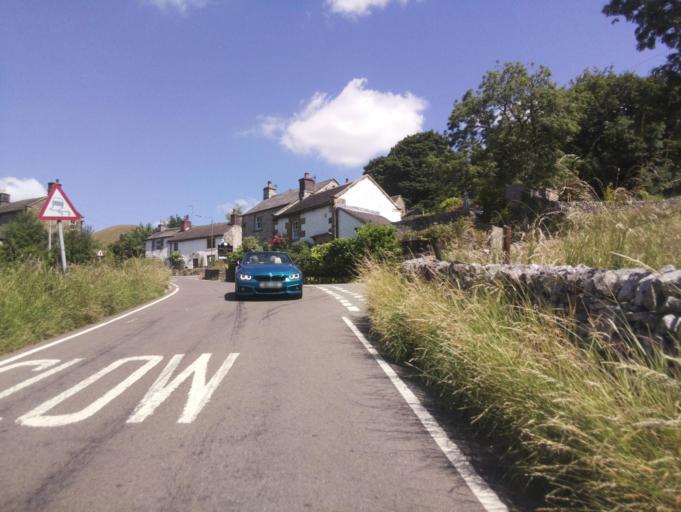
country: GB
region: England
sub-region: Derbyshire
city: Buxton
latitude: 53.1833
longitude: -1.8506
